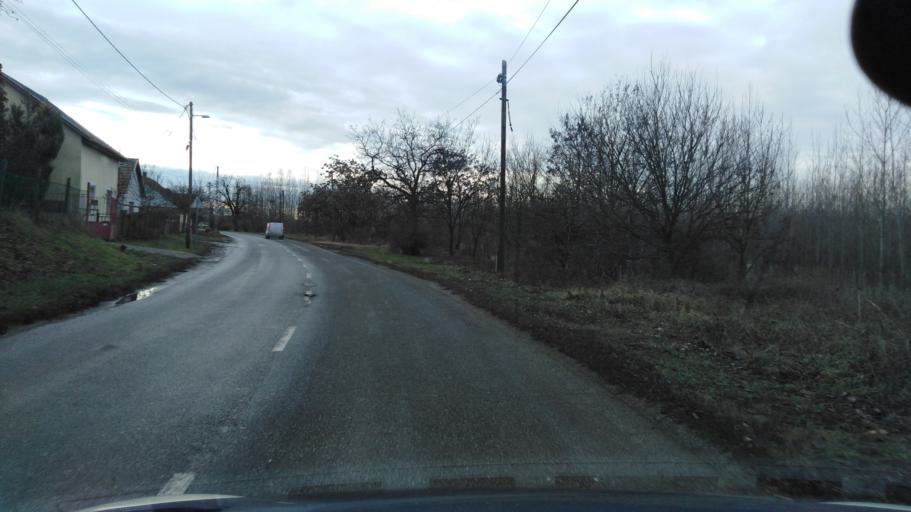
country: HU
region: Heves
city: Hatvan
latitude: 47.6859
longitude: 19.6894
